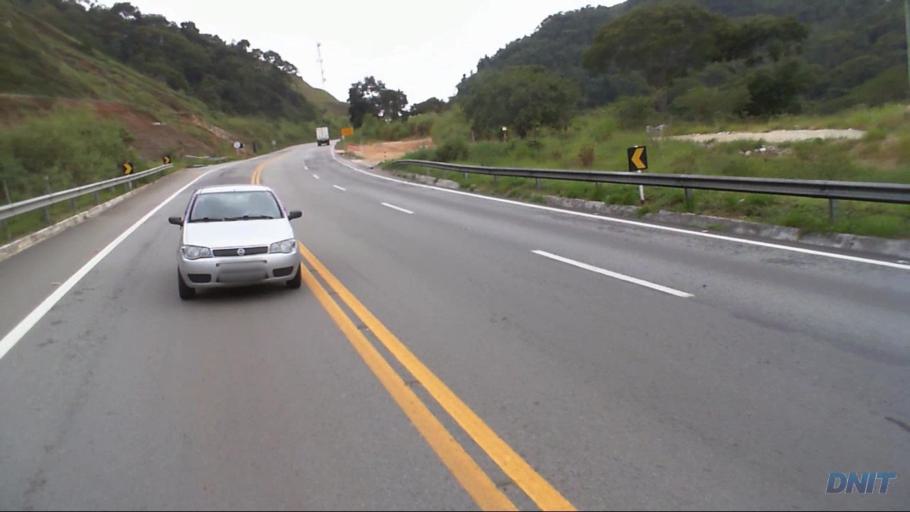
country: BR
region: Minas Gerais
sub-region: Nova Era
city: Nova Era
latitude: -19.6528
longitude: -42.9512
